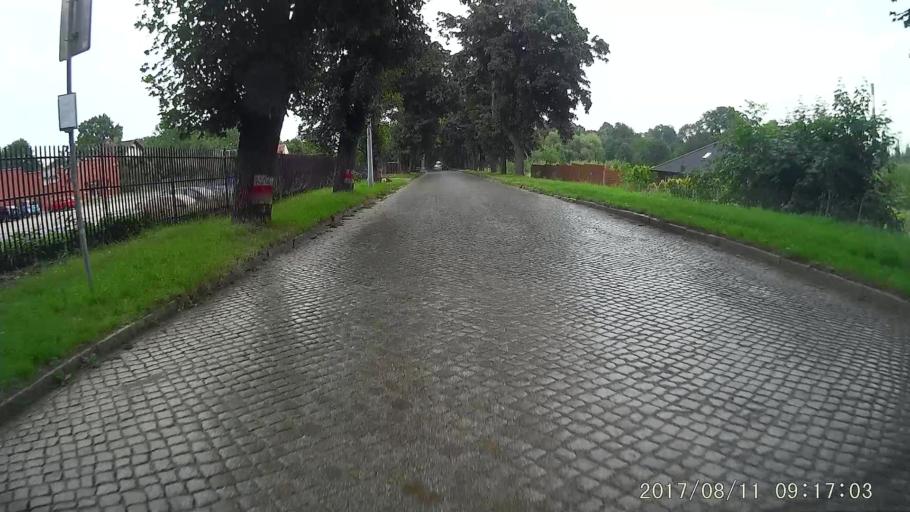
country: PL
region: Lower Silesian Voivodeship
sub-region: Powiat zgorzelecki
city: Zgorzelec
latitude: 51.1635
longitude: 15.0036
